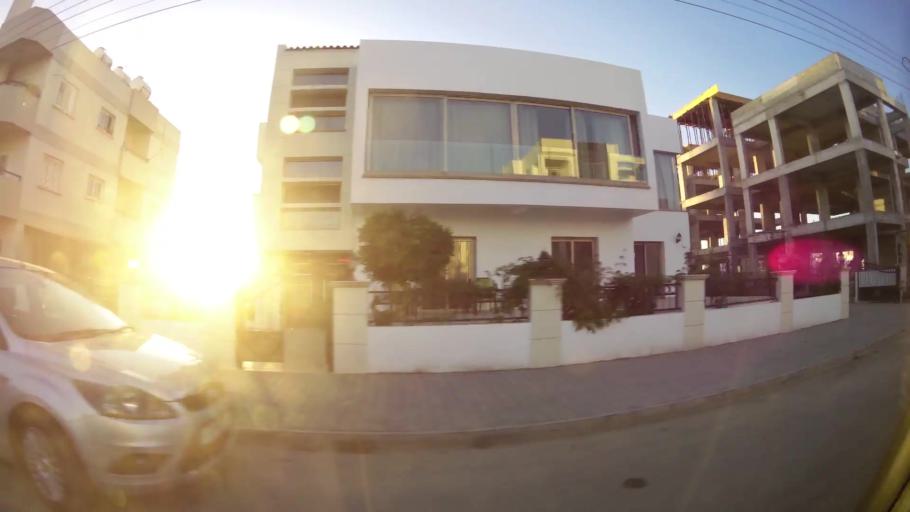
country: CY
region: Lefkosia
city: Nicosia
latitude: 35.2021
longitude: 33.3238
